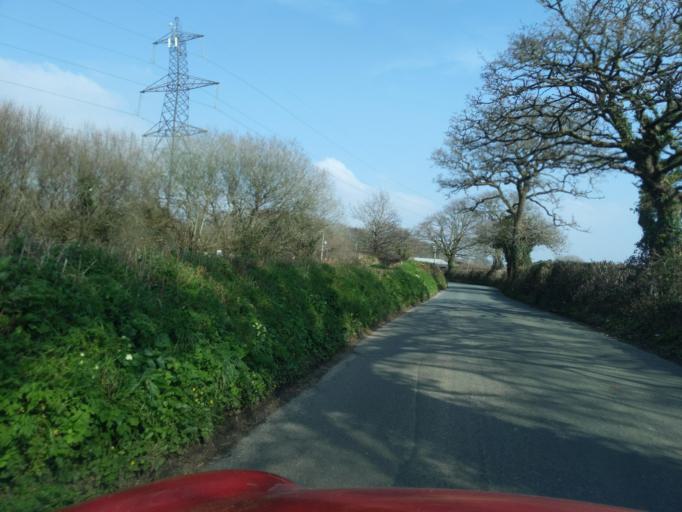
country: GB
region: England
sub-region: Devon
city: Ivybridge
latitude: 50.3829
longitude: -3.9144
